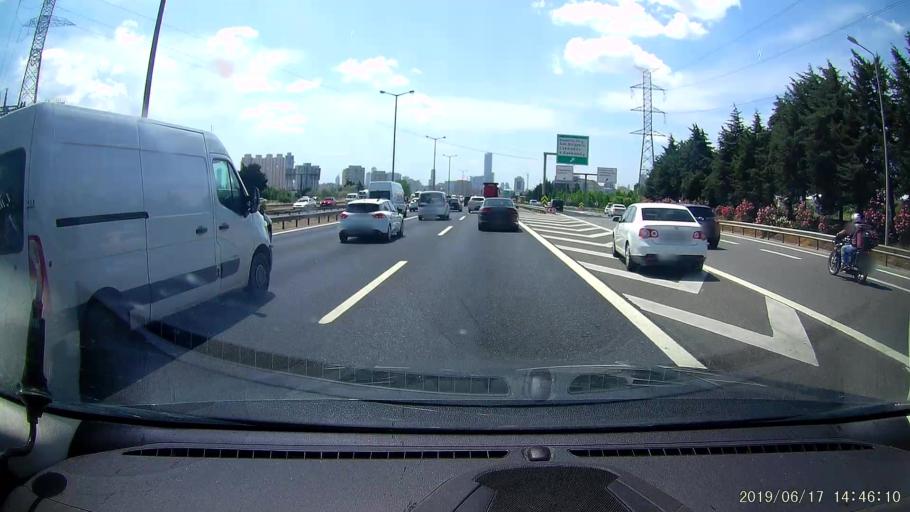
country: TR
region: Istanbul
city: Umraniye
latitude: 40.9950
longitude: 29.1588
